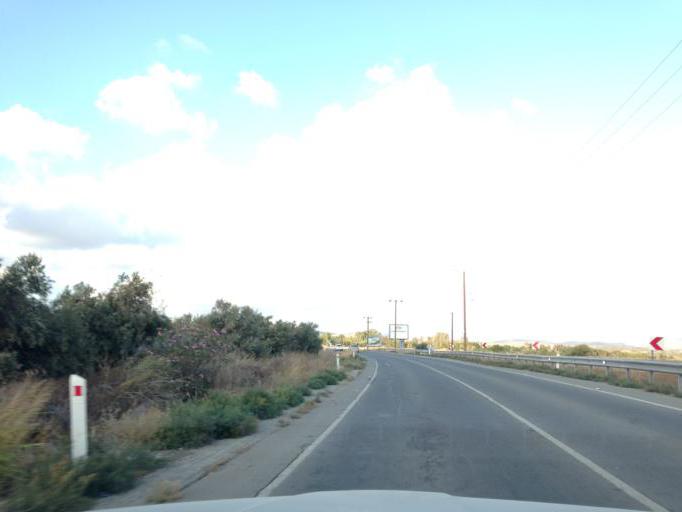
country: CY
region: Pafos
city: Paphos
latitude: 34.7104
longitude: 32.5098
